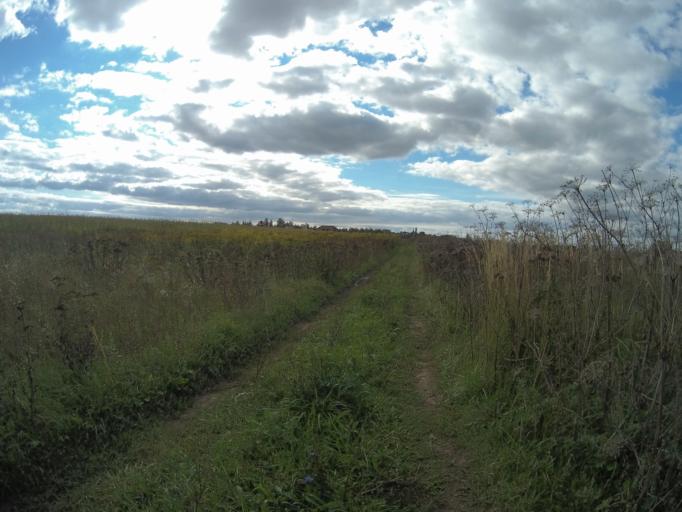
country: RU
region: Vladimir
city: Orgtrud
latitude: 56.3207
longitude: 40.6592
